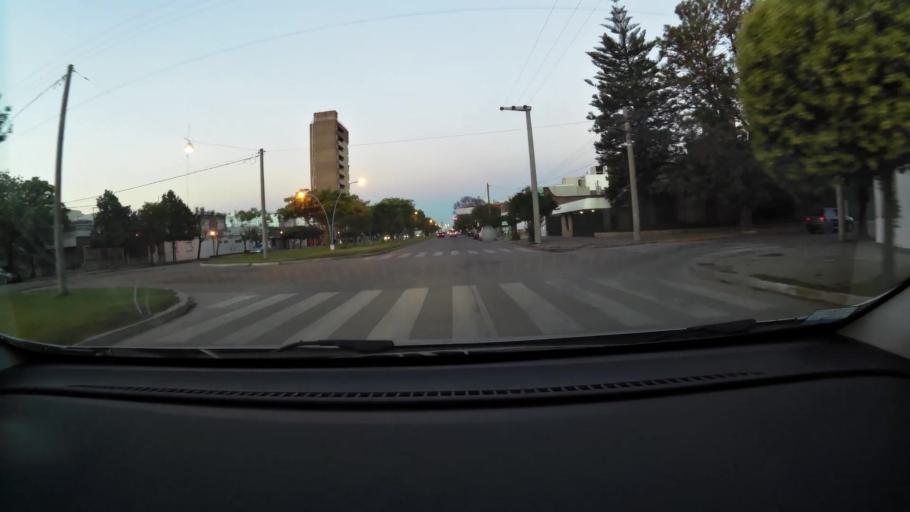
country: AR
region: Cordoba
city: Villa Maria
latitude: -32.4173
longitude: -63.2365
